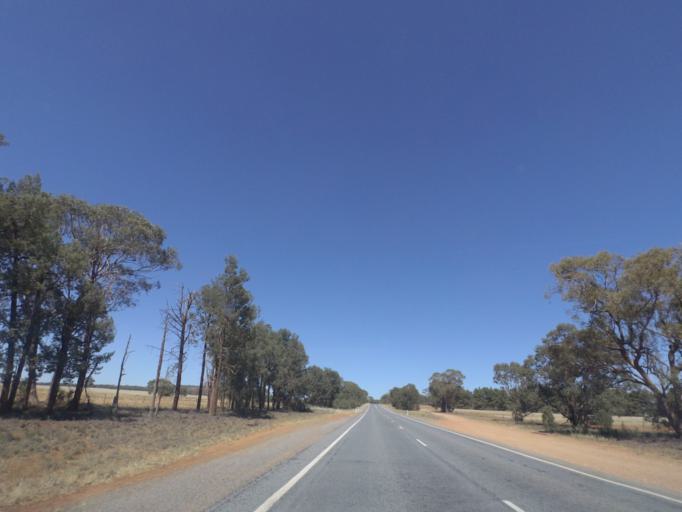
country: AU
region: New South Wales
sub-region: Narrandera
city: Narrandera
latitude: -34.4172
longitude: 146.8547
